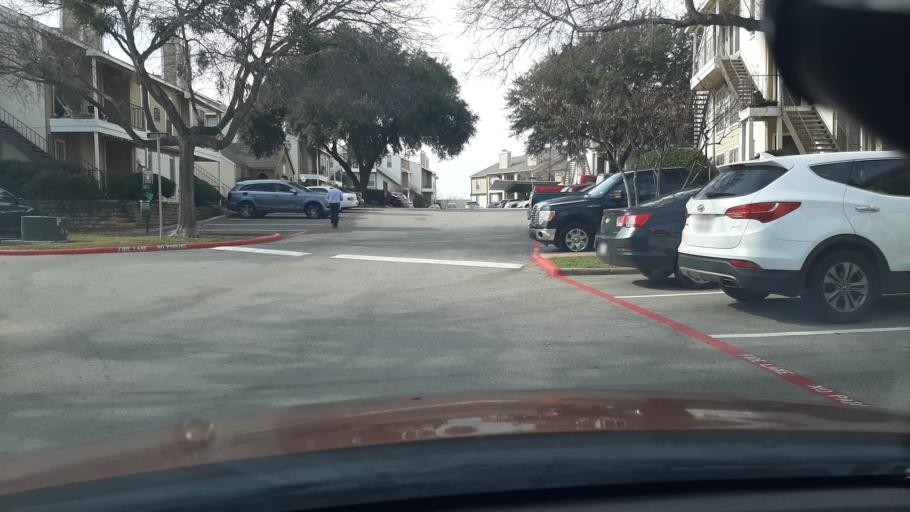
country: US
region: Texas
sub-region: Tarrant County
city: Benbrook
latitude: 32.6624
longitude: -97.4092
